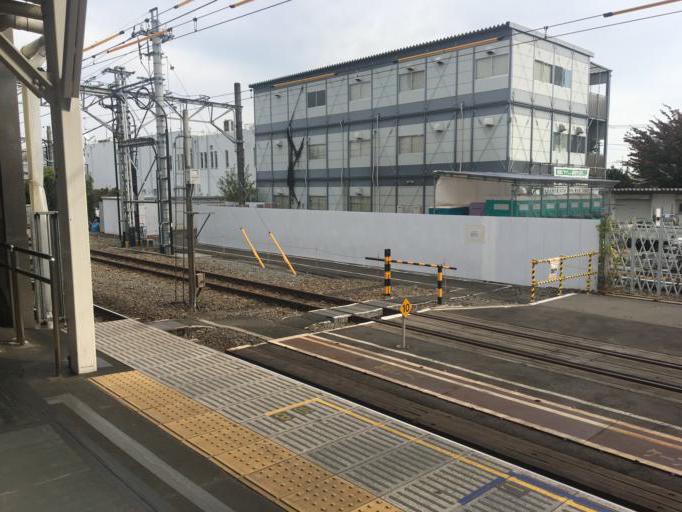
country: JP
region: Saitama
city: Tokorozawa
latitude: 35.7879
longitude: 139.4737
